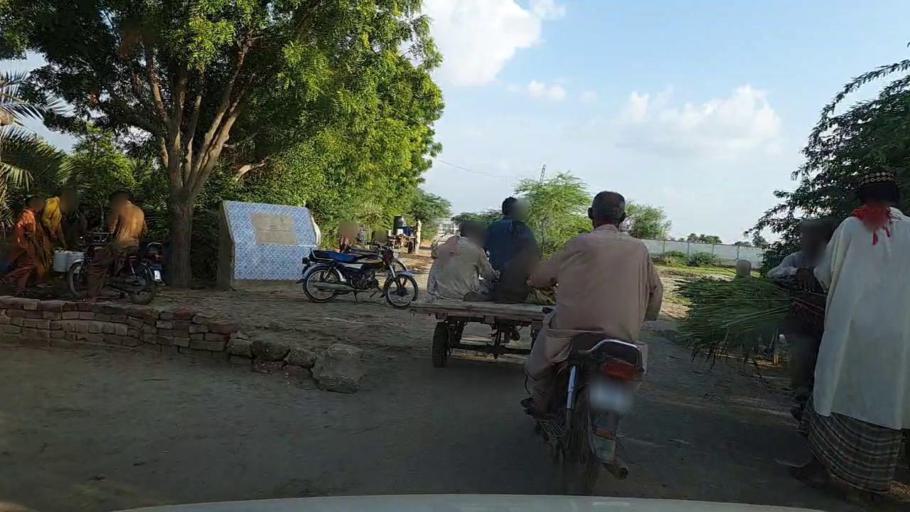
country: PK
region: Sindh
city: Hingorja
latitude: 27.0880
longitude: 68.4180
